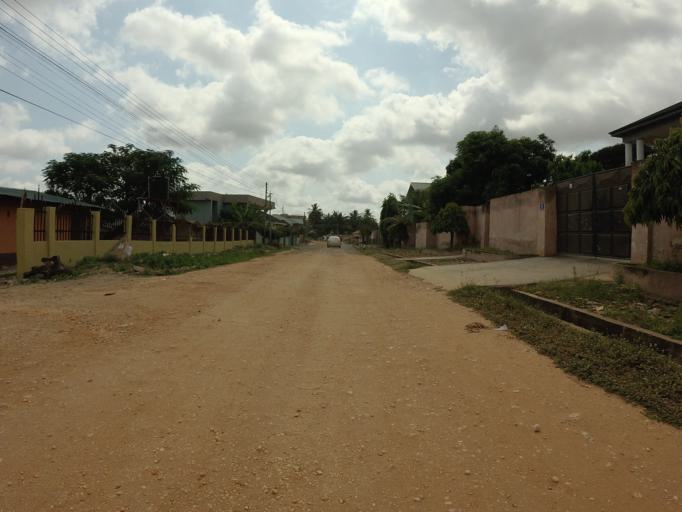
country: GH
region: Greater Accra
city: Dome
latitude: 5.6195
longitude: -0.2439
